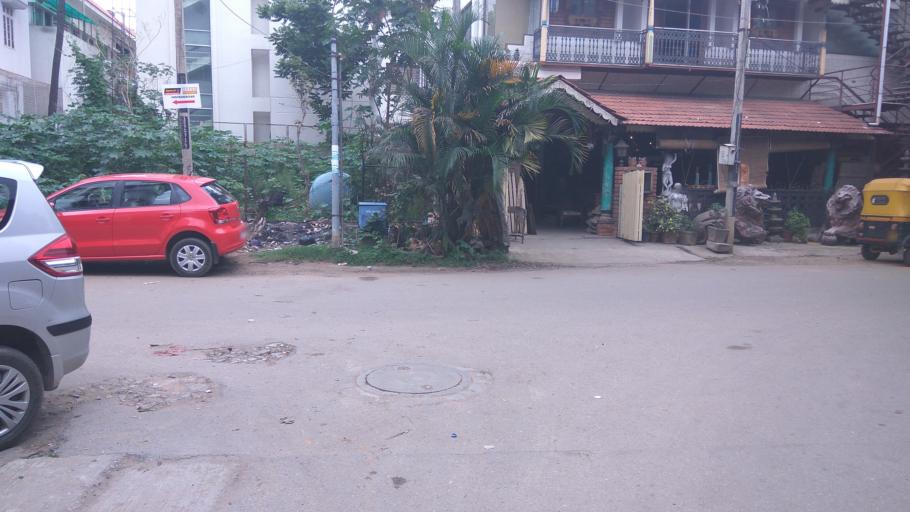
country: IN
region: Karnataka
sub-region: Bangalore Urban
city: Bangalore
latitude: 12.9638
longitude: 77.6409
